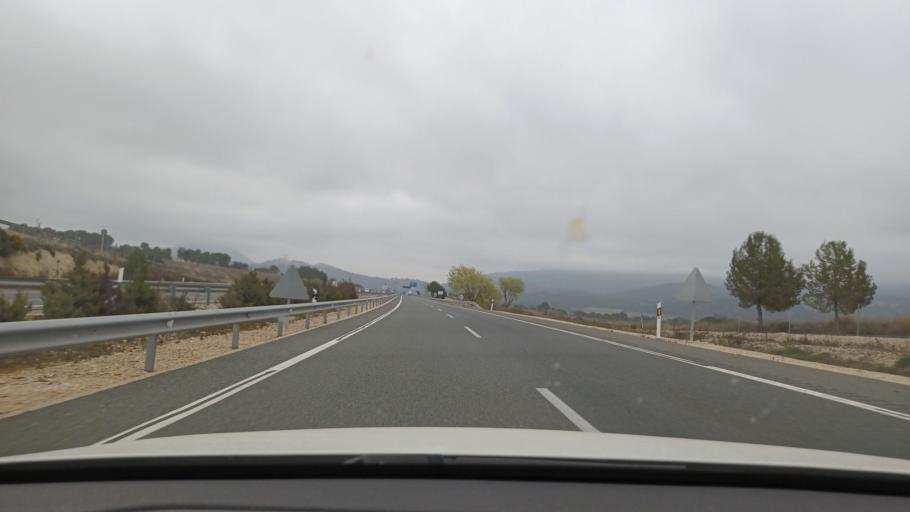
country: ES
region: Valencia
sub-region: Provincia de Alicante
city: Alcoy
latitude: 38.6416
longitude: -0.4907
